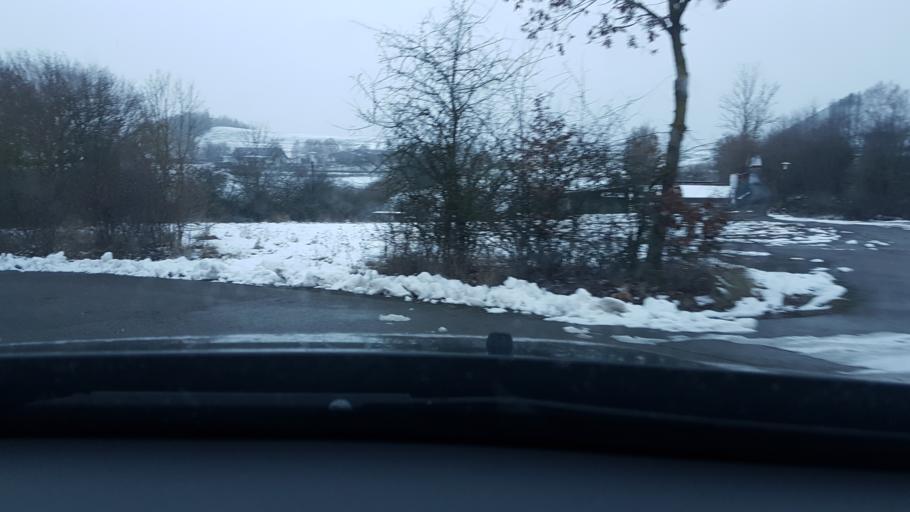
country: DE
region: North Rhine-Westphalia
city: Marsberg
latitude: 51.3641
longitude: 8.8085
